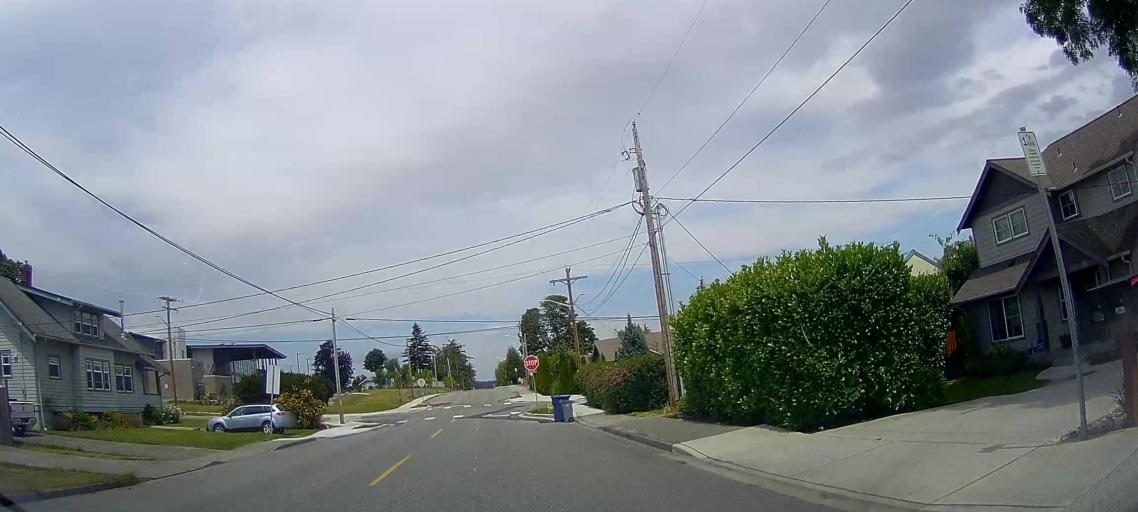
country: US
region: Washington
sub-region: Skagit County
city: Anacortes
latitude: 48.5058
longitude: -122.6206
